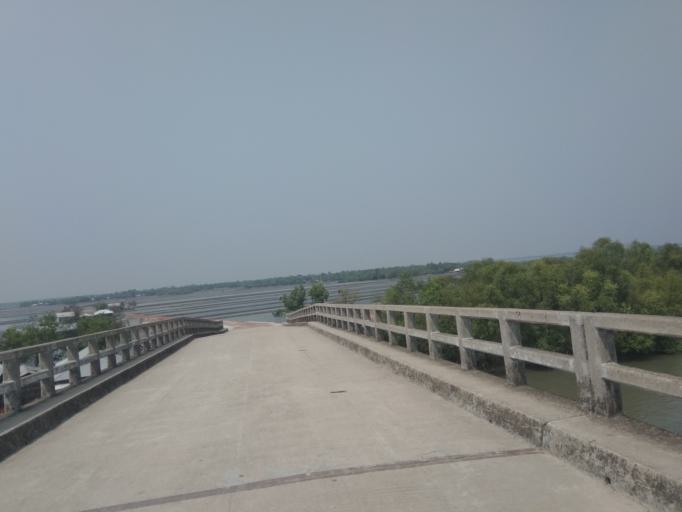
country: IN
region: West Bengal
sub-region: North 24 Parganas
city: Taki
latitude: 22.2889
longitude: 89.2737
